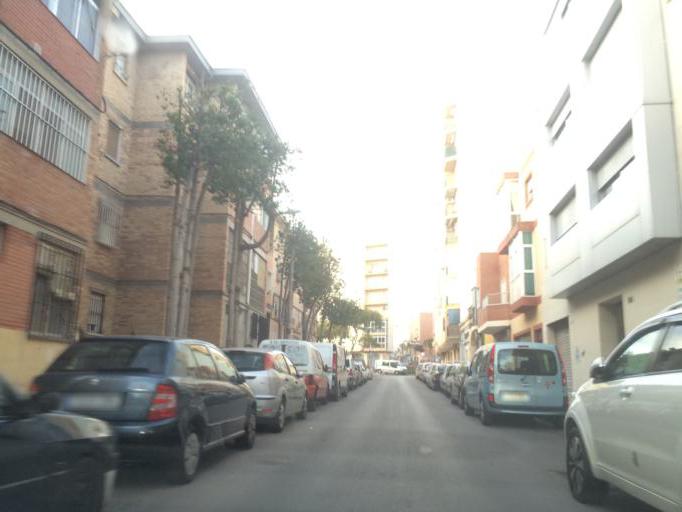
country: ES
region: Andalusia
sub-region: Provincia de Almeria
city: Almeria
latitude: 36.8455
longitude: -2.4665
